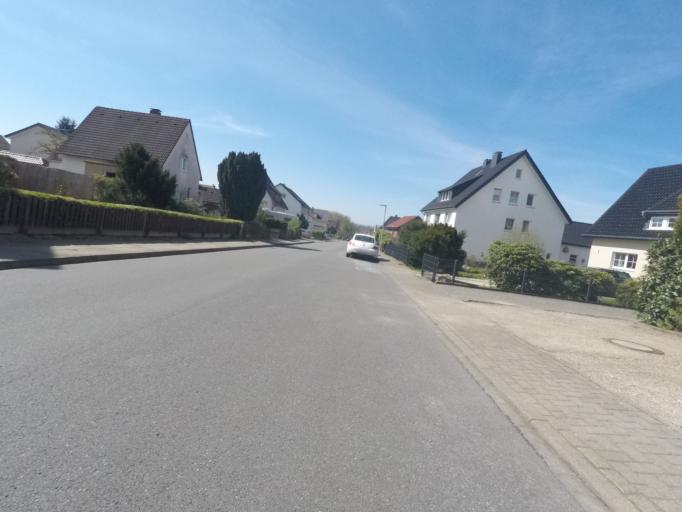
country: DE
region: North Rhine-Westphalia
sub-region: Regierungsbezirk Detmold
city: Herford
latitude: 52.0621
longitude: 8.6222
